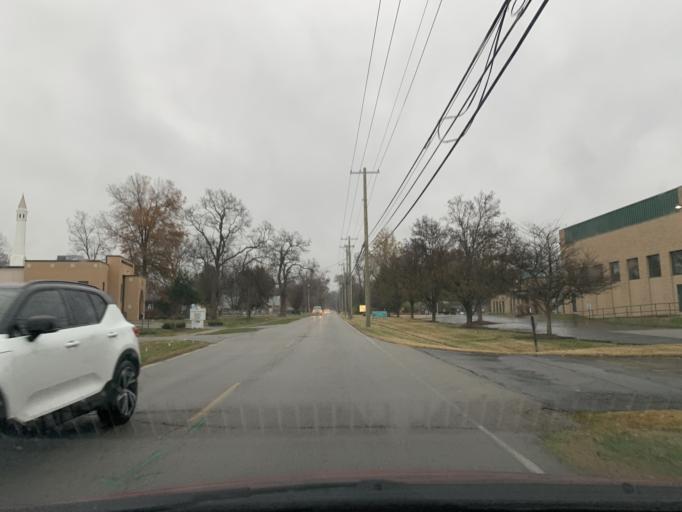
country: US
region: Kentucky
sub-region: Jefferson County
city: Buechel
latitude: 38.1960
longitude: -85.6506
